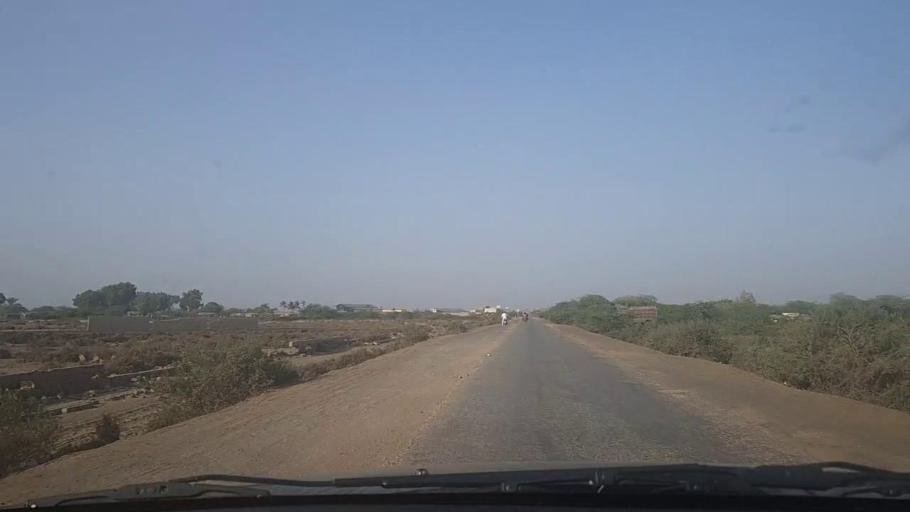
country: PK
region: Sindh
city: Keti Bandar
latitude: 24.3097
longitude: 67.6088
